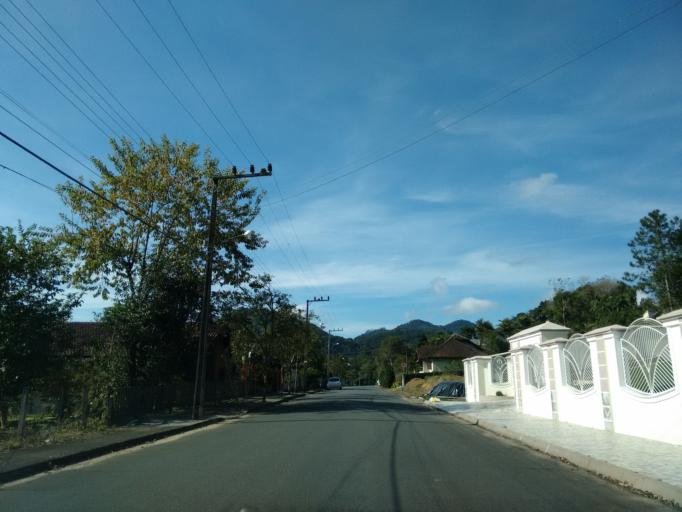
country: BR
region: Santa Catarina
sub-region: Pomerode
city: Pomerode
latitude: -26.7558
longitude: -49.1773
